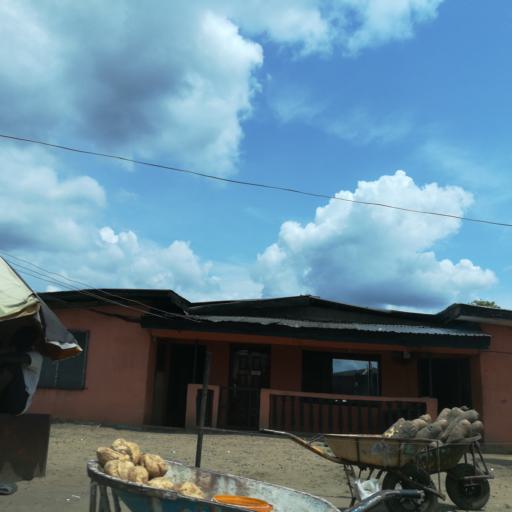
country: NG
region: Rivers
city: Port Harcourt
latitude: 4.7804
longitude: 7.0584
